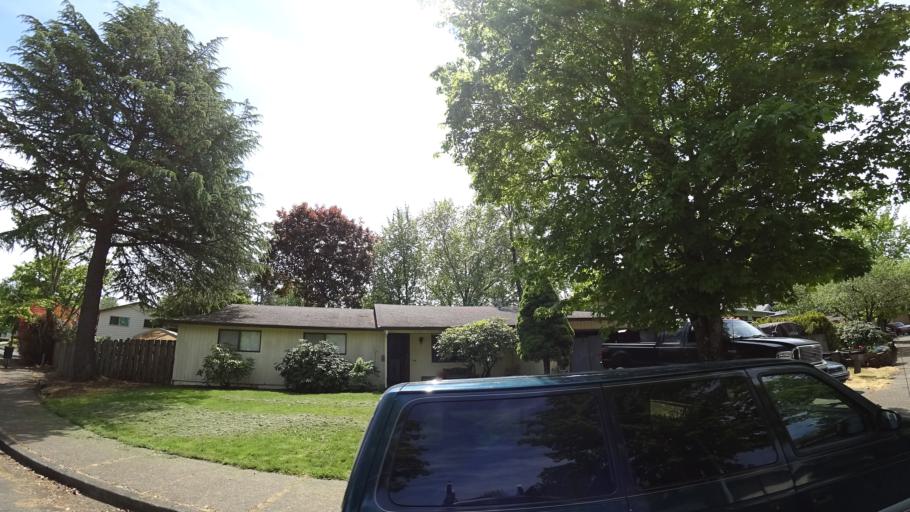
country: US
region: Oregon
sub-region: Washington County
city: Aloha
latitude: 45.4721
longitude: -122.8934
